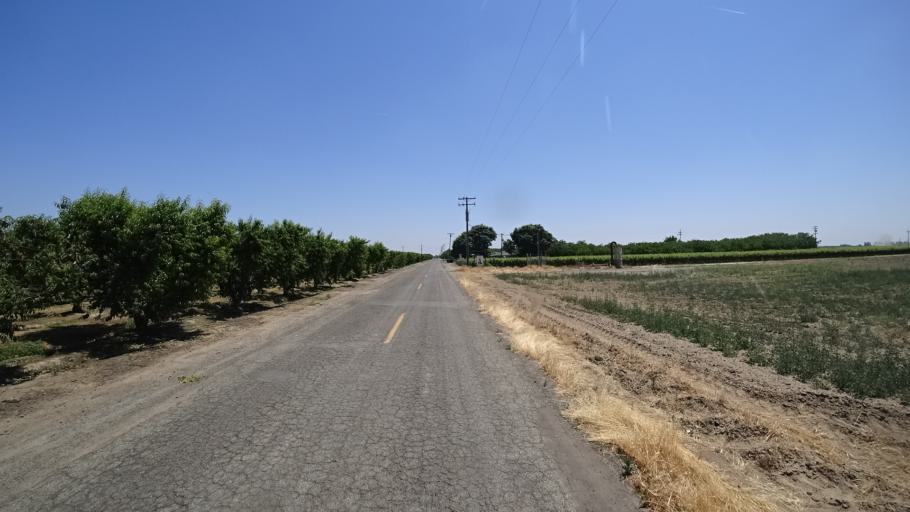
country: US
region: California
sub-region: Fresno County
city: Laton
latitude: 36.3865
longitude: -119.7579
